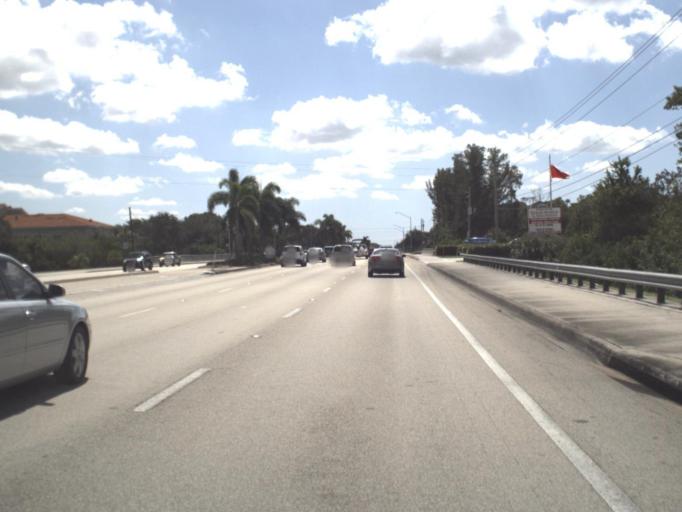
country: US
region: Florida
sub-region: Collier County
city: Naples Park
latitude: 26.2841
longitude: -81.8020
